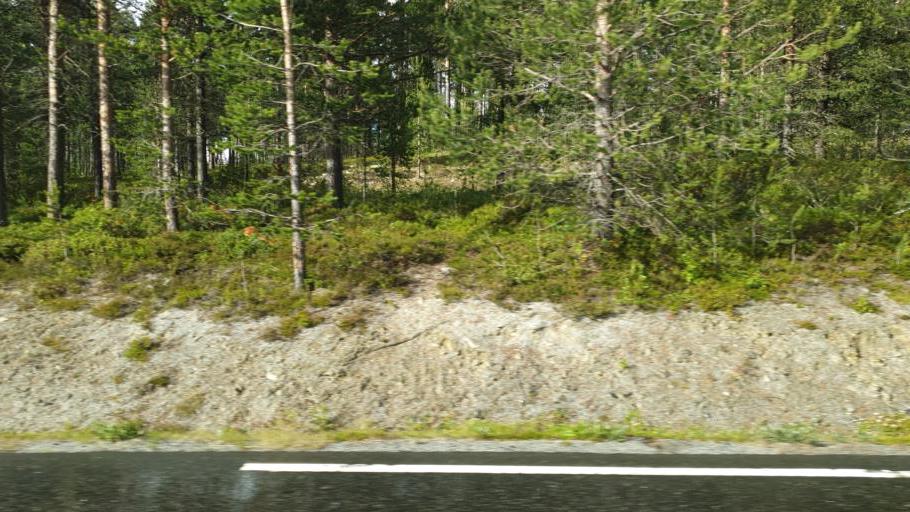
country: NO
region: Oppland
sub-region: Vaga
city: Vagamo
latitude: 61.8168
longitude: 8.9853
